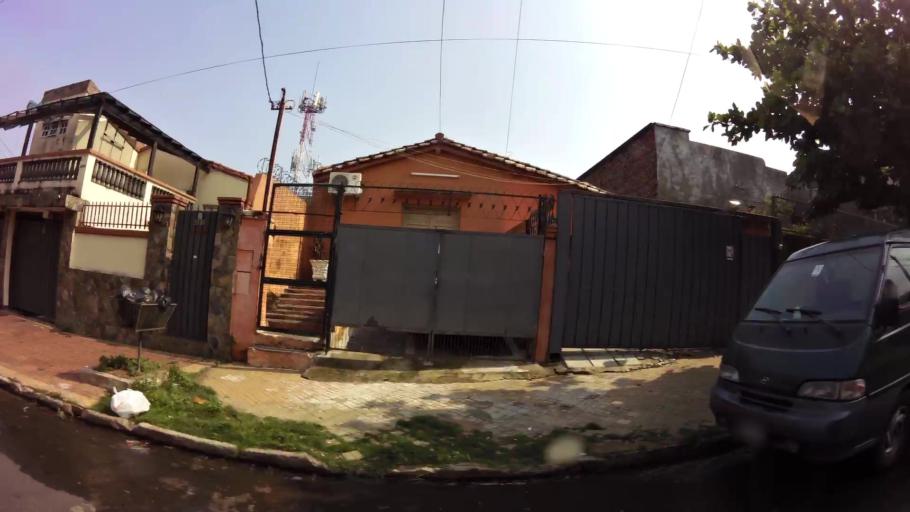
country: PY
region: Presidente Hayes
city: Nanawa
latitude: -25.2931
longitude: -57.6638
